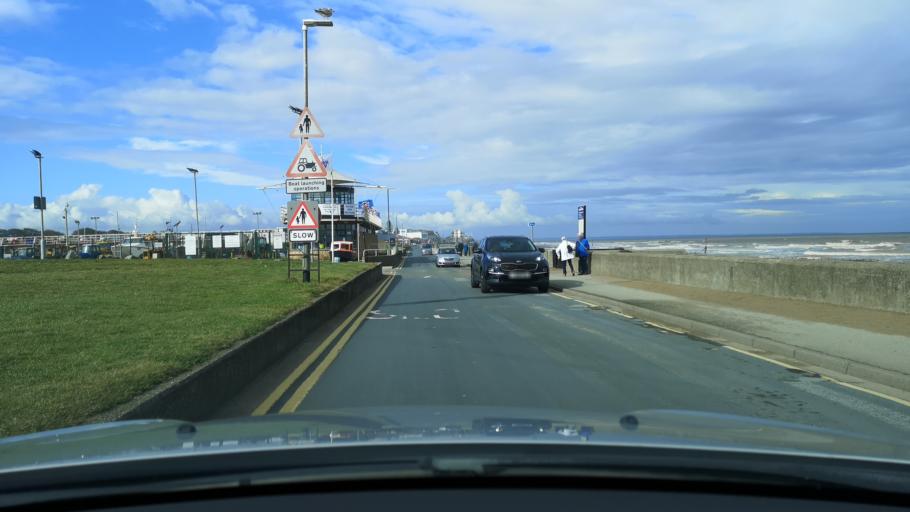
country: GB
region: England
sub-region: East Riding of Yorkshire
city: Hornsea
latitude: 53.9080
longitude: -0.1579
